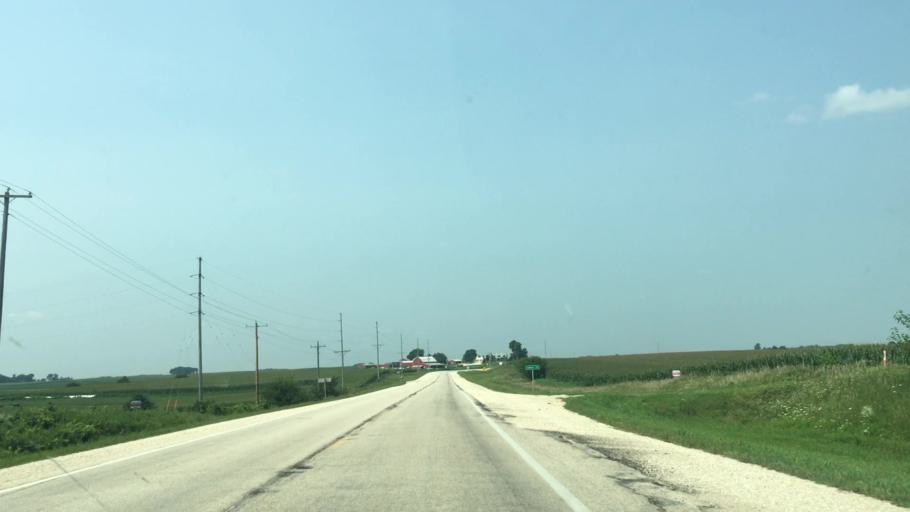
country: US
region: Iowa
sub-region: Fayette County
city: West Union
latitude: 42.9746
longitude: -91.8200
